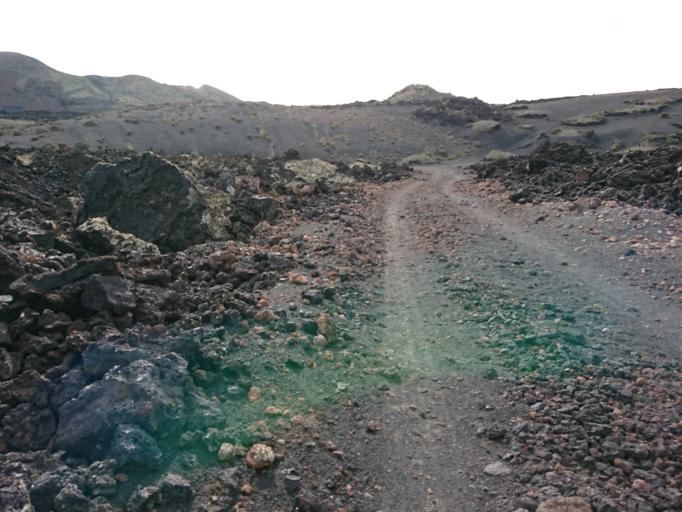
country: ES
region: Canary Islands
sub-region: Provincia de Las Palmas
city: Tinajo
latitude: 29.0139
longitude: -13.6779
